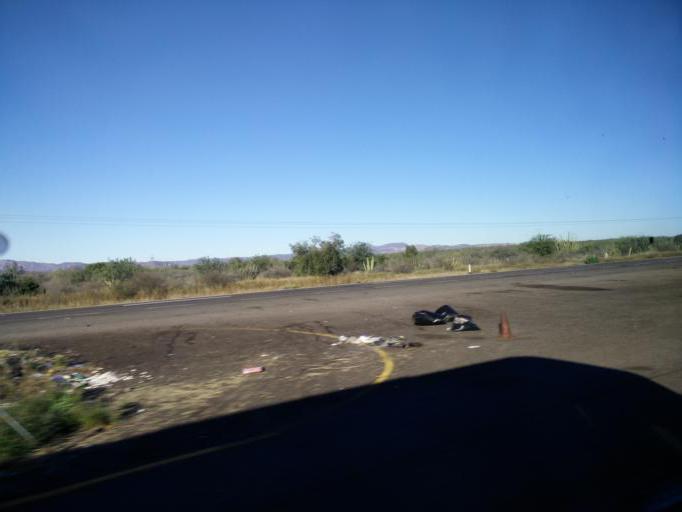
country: MX
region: Sonora
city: Heroica Guaymas
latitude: 28.1349
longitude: -110.9718
